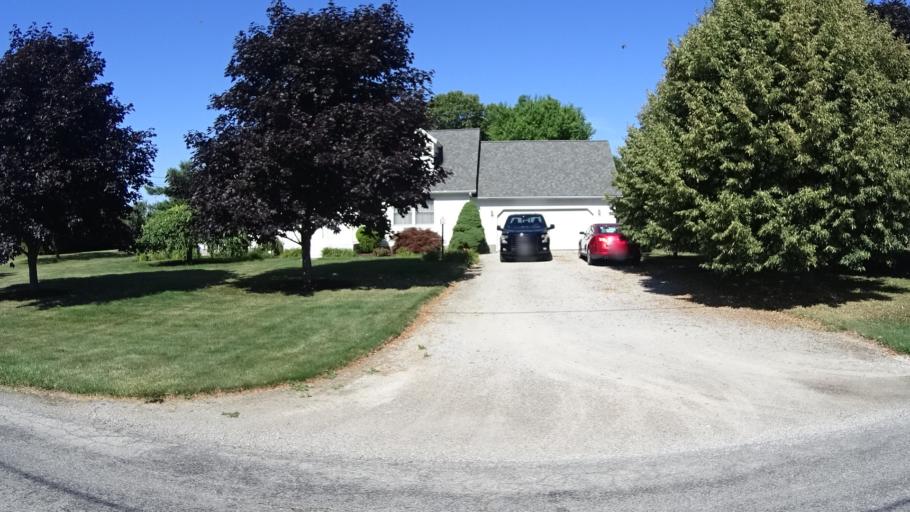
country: US
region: Ohio
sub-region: Erie County
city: Sandusky
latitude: 41.3844
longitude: -82.7102
